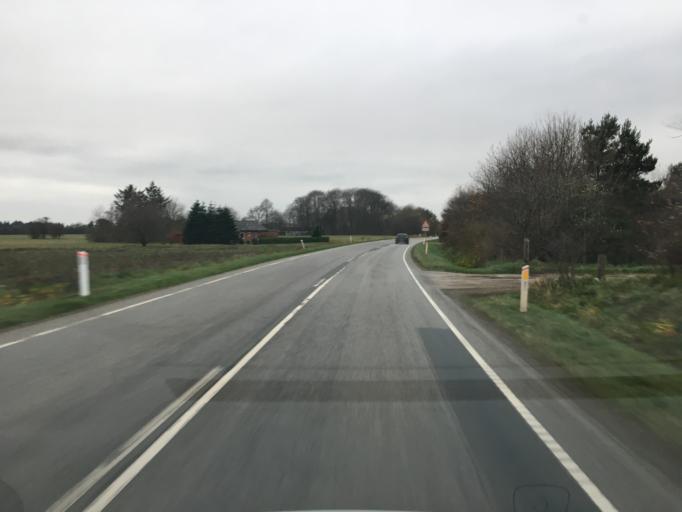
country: DK
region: South Denmark
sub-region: Aabenraa Kommune
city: Tinglev
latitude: 54.9776
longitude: 9.1492
